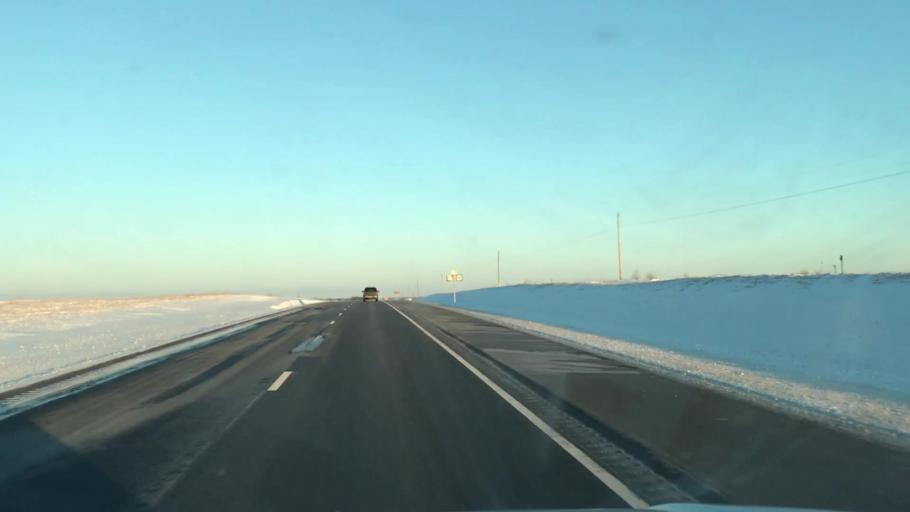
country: US
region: Missouri
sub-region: DeKalb County
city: Maysville
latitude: 39.7615
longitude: -94.3680
